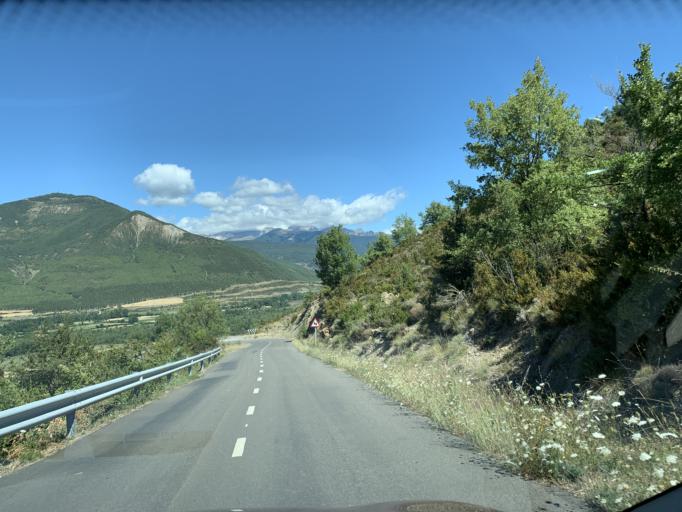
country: ES
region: Aragon
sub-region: Provincia de Huesca
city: Sabinanigo
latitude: 42.5460
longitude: -0.3174
